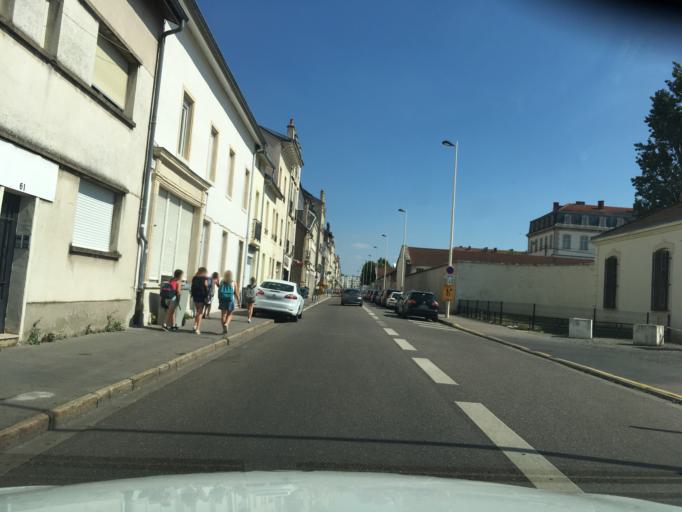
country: FR
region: Lorraine
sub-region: Departement de Meurthe-et-Moselle
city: Nancy
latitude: 48.6774
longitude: 6.1687
